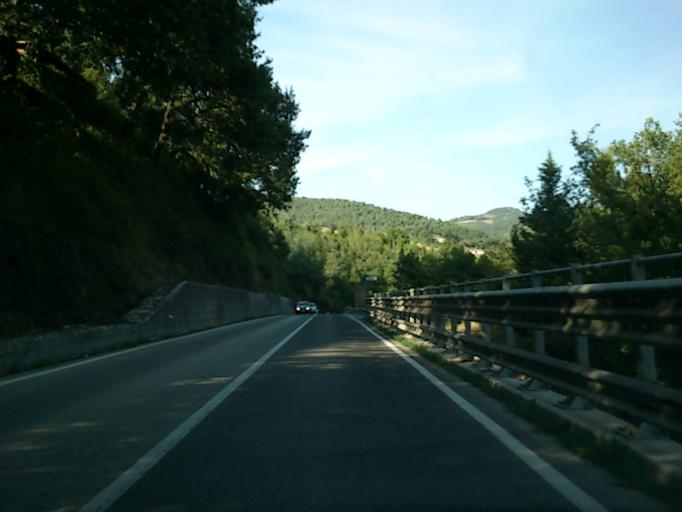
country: IT
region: The Marches
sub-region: Provincia di Pesaro e Urbino
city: Canavaccio
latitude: 43.6981
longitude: 12.6782
